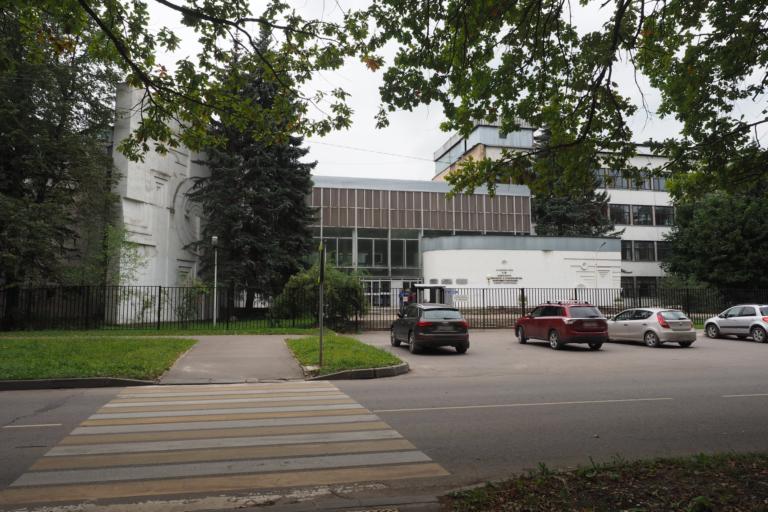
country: RU
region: Moskovskaya
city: Pushchino
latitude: 54.8312
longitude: 37.6202
